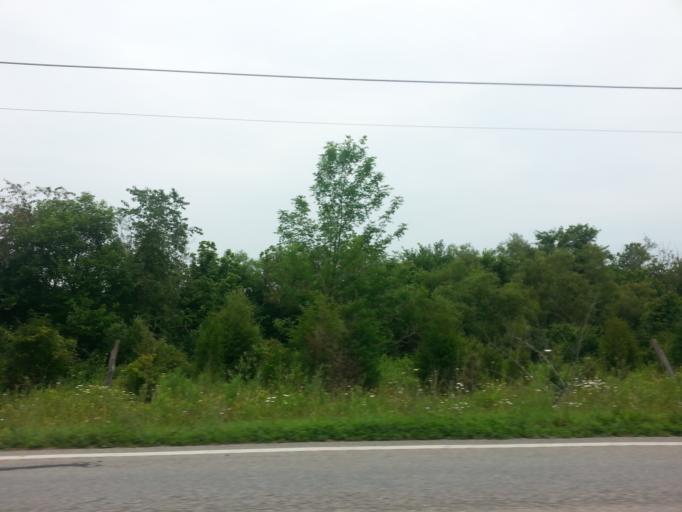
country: US
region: Ohio
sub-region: Brown County
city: Mount Orab
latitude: 38.9965
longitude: -83.9211
